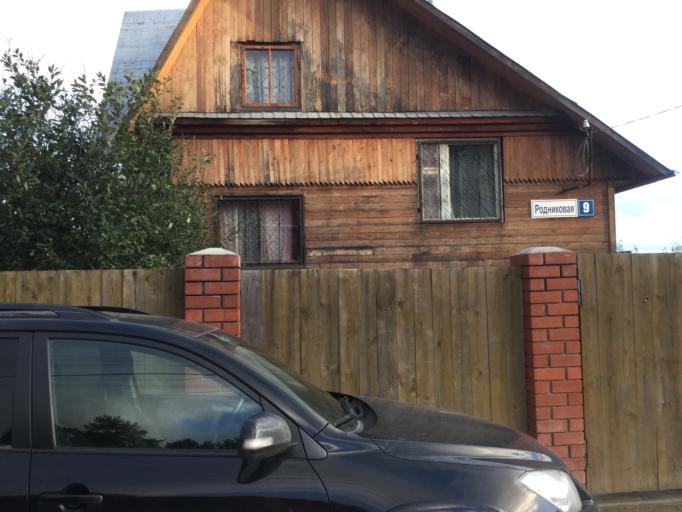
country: RU
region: Sverdlovsk
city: Iset'
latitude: 57.0337
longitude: 60.4040
